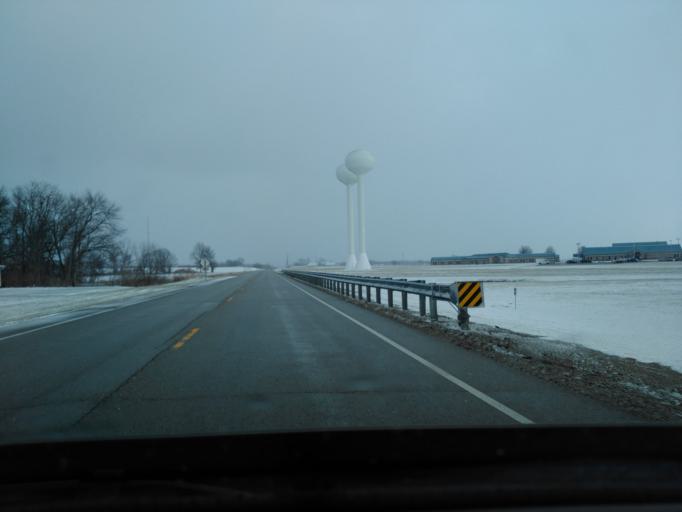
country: US
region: Illinois
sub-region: Bond County
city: Greenville
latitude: 38.8701
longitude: -89.4130
